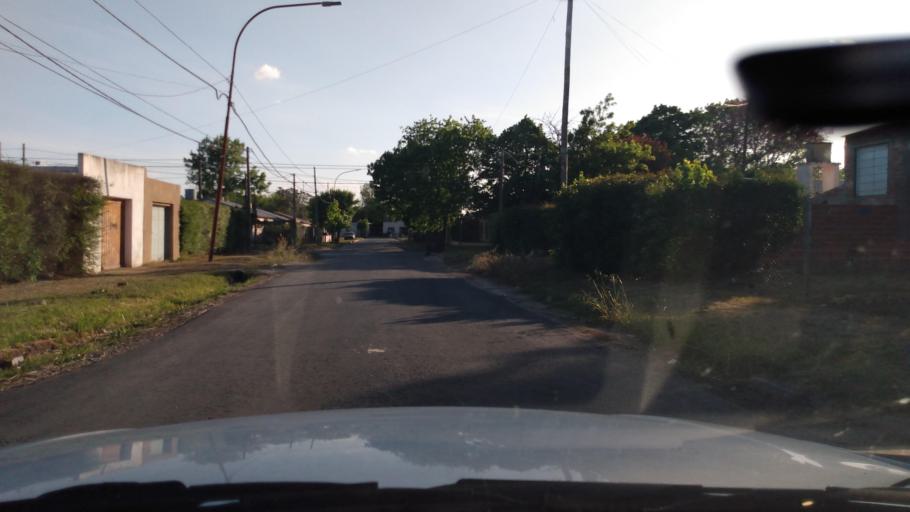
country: AR
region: Buenos Aires
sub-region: Partido de Lujan
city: Lujan
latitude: -34.5792
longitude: -59.1164
